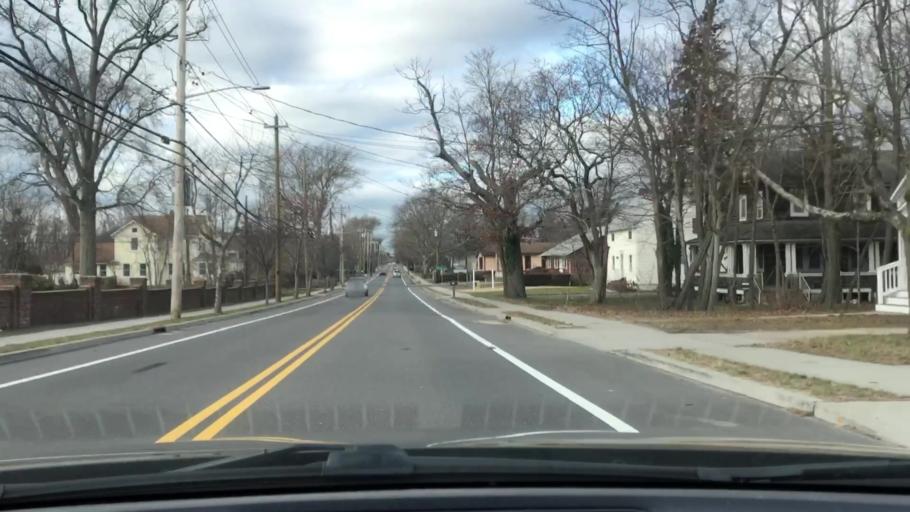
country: US
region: New York
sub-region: Suffolk County
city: Riverhead
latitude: 40.9266
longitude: -72.6688
